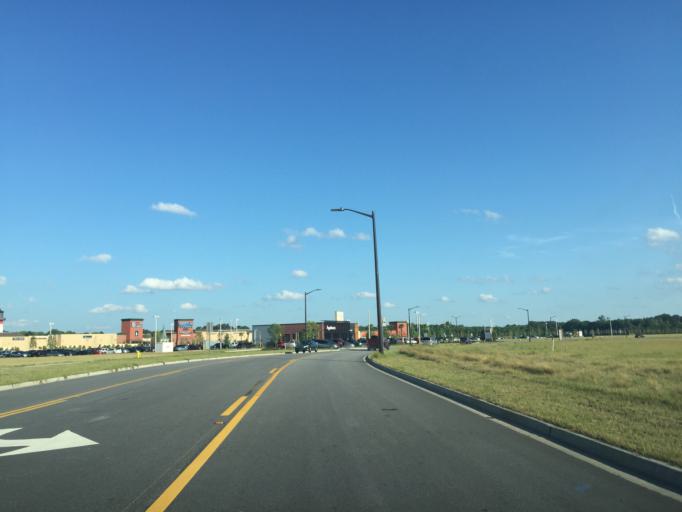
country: US
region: Georgia
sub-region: Chatham County
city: Pooler
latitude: 32.1368
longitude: -81.2466
